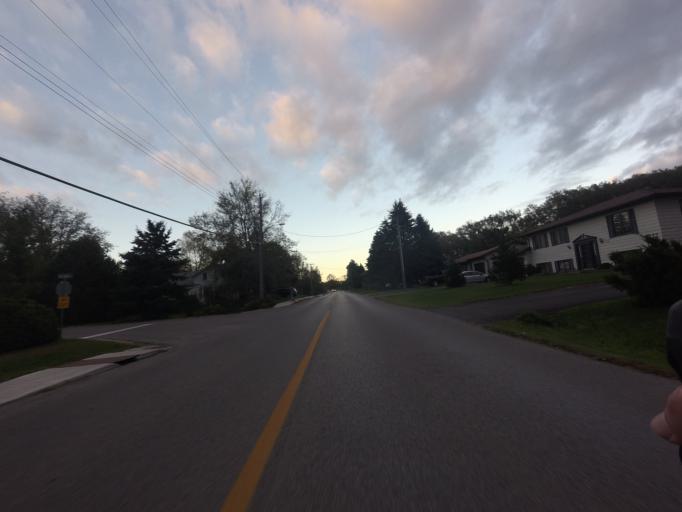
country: CA
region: Ontario
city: Quinte West
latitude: 44.0272
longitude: -77.7250
